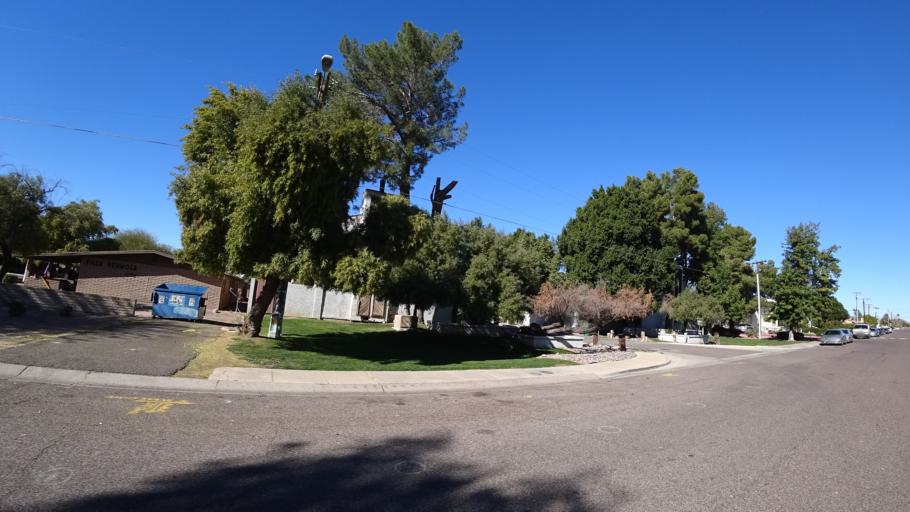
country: US
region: Arizona
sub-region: Maricopa County
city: Phoenix
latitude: 33.5215
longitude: -112.0607
